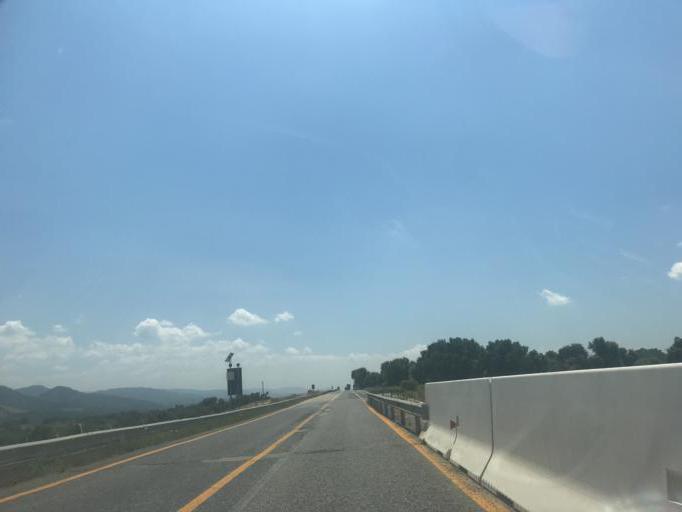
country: IT
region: Sardinia
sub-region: Provincia di Olbia-Tempio
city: Monti
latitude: 40.8026
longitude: 9.2800
